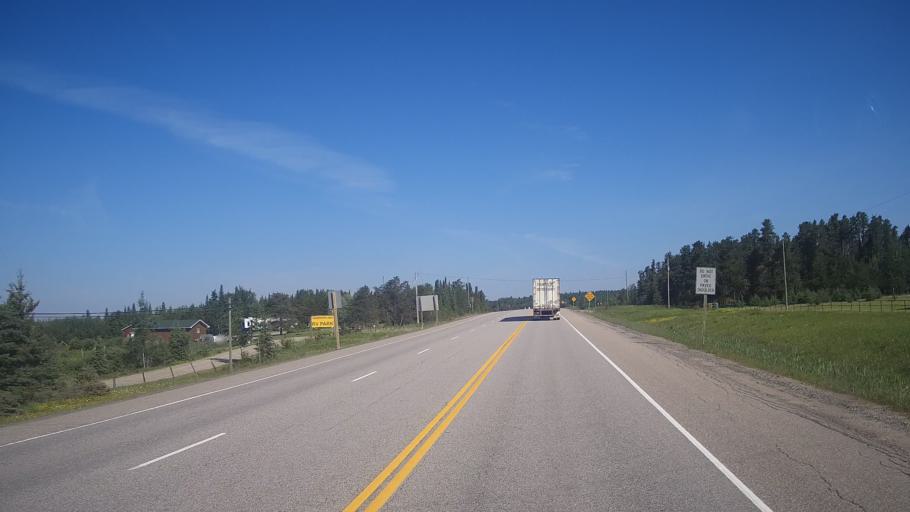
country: CA
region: Ontario
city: Dryden
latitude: 49.7143
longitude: -92.5928
